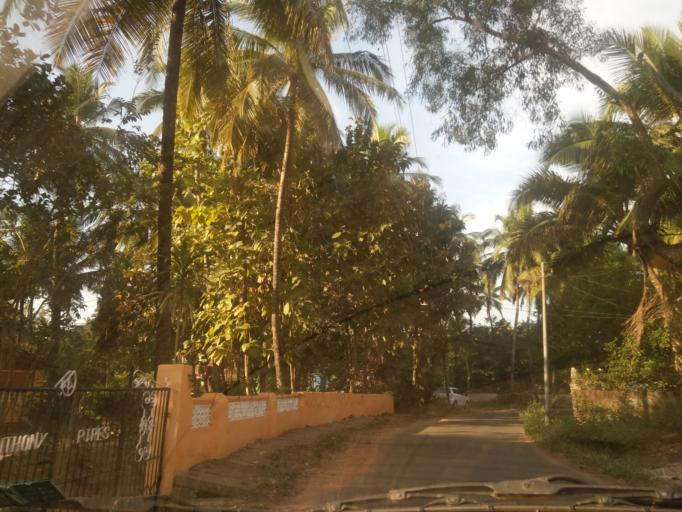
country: IN
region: Goa
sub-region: South Goa
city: Varca
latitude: 15.2415
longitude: 73.9692
